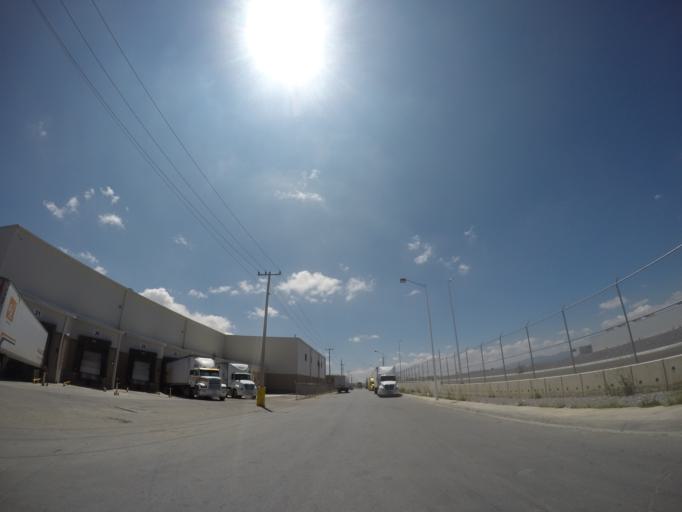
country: MX
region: San Luis Potosi
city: La Pila
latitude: 21.9752
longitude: -100.8791
